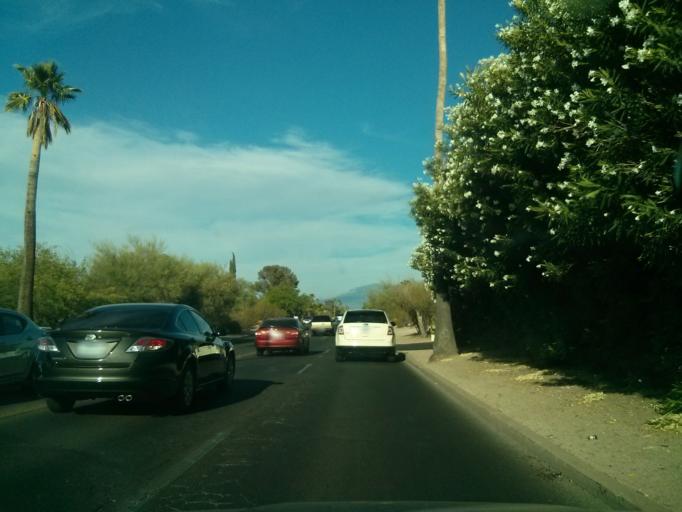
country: US
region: Arizona
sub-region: Pima County
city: Tucson
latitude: 32.2288
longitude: -110.9245
